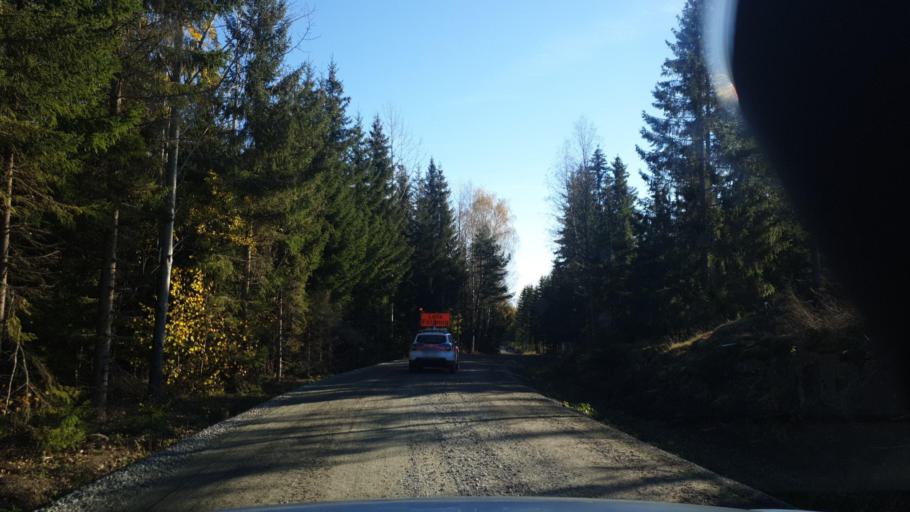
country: SE
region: Vaermland
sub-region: Karlstads Kommun
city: Valberg
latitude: 59.4144
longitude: 13.1602
